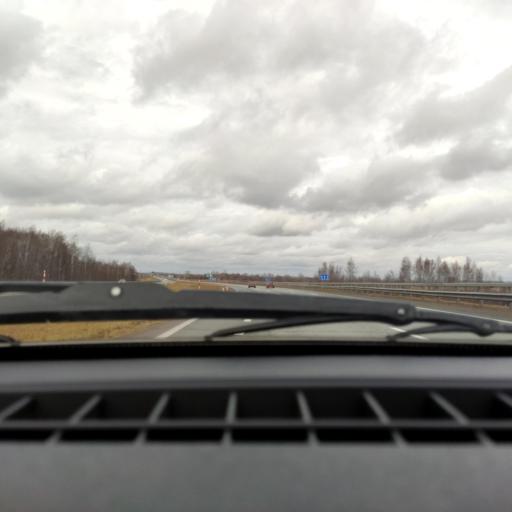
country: RU
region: Bashkortostan
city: Asanovo
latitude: 54.9648
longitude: 55.5835
